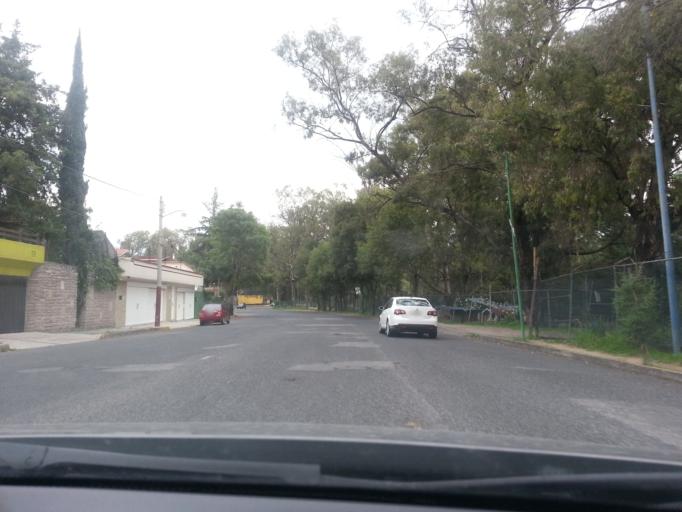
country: MX
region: Mexico
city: Ciudad Lopez Mateos
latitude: 19.6195
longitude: -99.2457
